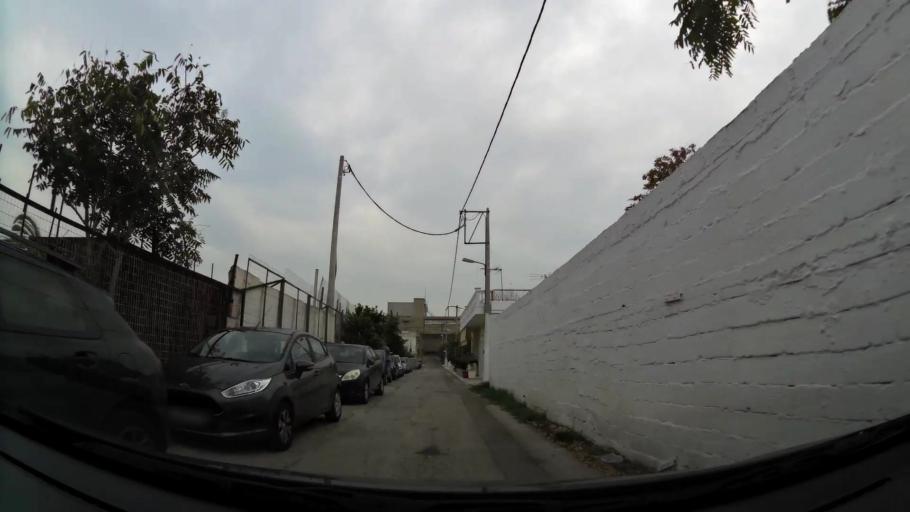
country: GR
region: Attica
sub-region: Nomos Piraios
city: Agios Ioannis Rentis
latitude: 37.9690
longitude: 23.6648
